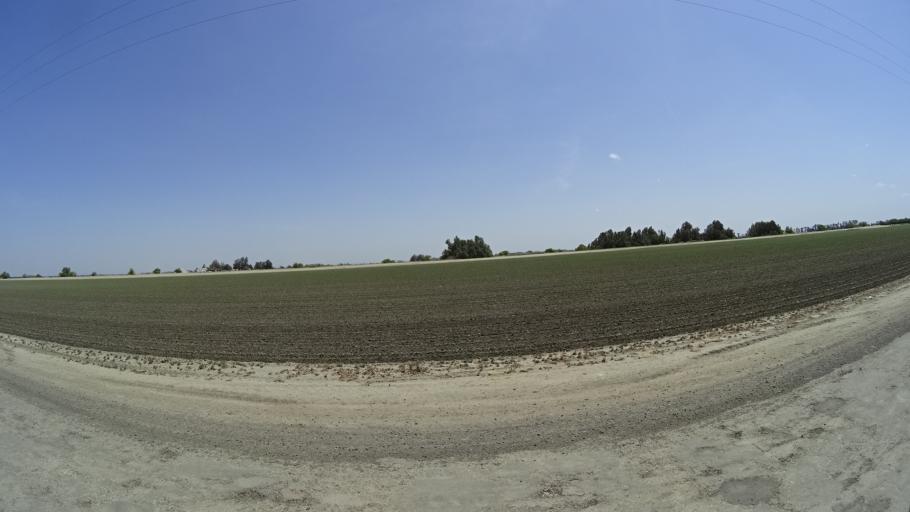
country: US
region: California
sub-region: Kings County
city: Stratford
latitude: 36.1999
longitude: -119.8515
